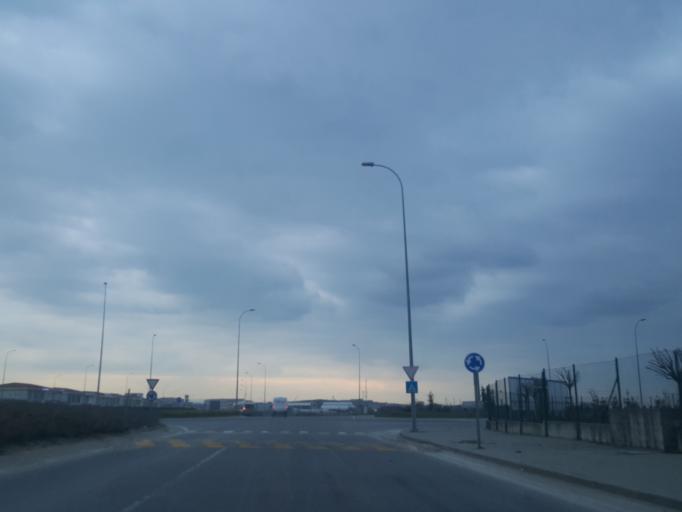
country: TR
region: Kocaeli
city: Tavsanli
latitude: 40.8324
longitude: 29.5714
